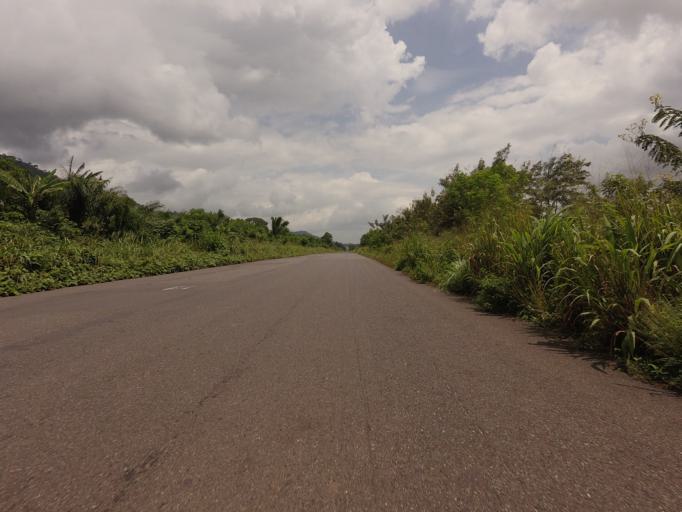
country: GH
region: Volta
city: Ho
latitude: 6.5672
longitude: 0.2697
